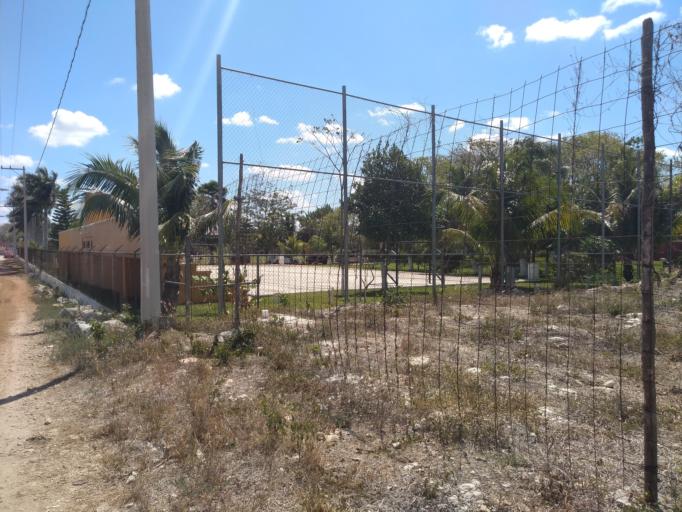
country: MX
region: Yucatan
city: Itzincab Palomeque
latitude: 20.9248
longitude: -89.6678
